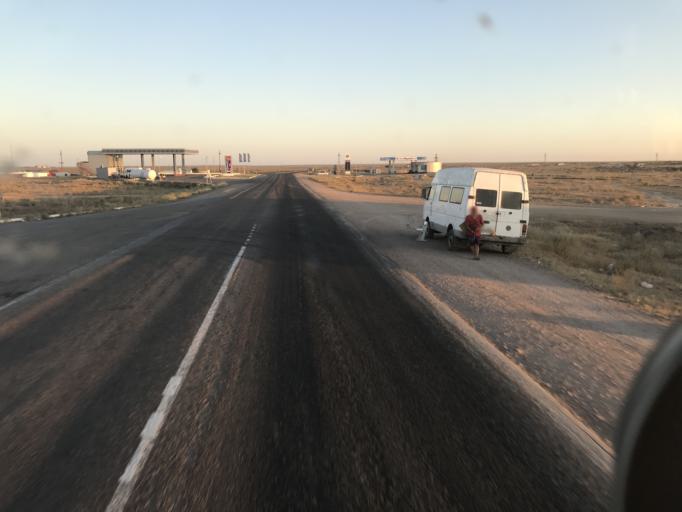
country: KZ
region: Qaraghandy
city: Saryshaghan
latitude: 46.0214
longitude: 73.5914
